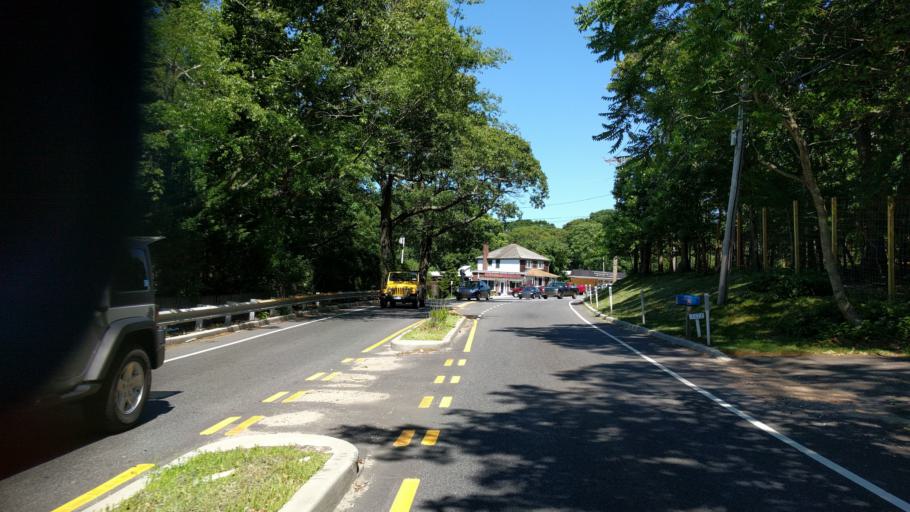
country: US
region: New York
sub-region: Suffolk County
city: Noyack
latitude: 40.9957
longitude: -72.3408
